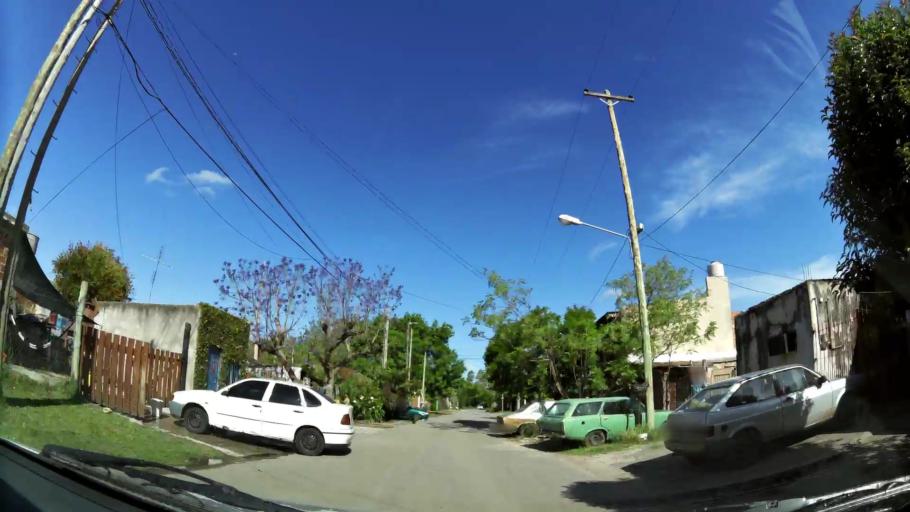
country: AR
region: Buenos Aires
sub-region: Partido de Quilmes
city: Quilmes
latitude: -34.7998
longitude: -58.2304
